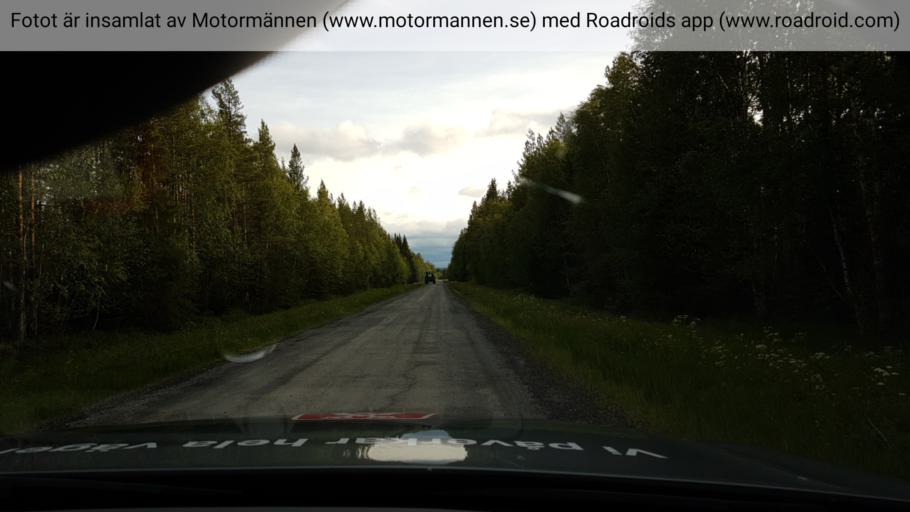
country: SE
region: Jaemtland
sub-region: Stroemsunds Kommun
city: Stroemsund
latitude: 63.7088
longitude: 15.1806
